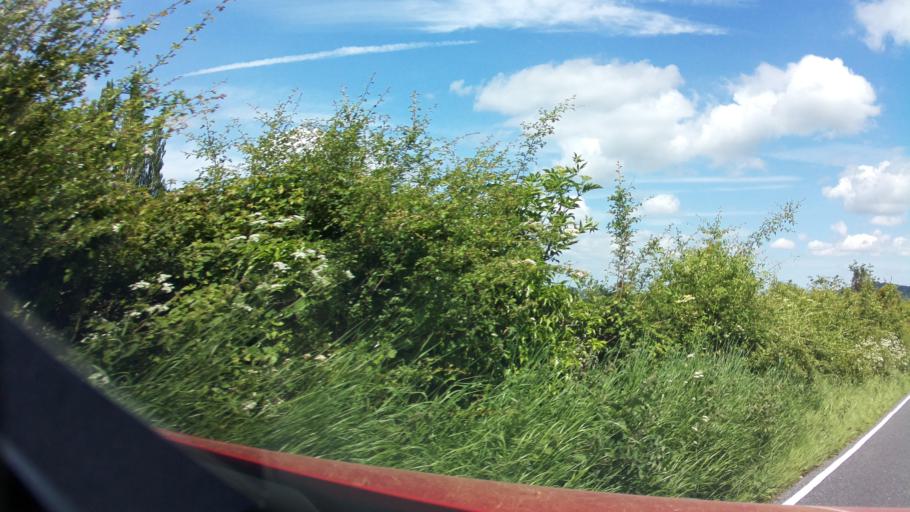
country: GB
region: Wales
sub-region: Monmouthshire
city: Mitchel Troy
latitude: 51.7826
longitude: -2.7225
